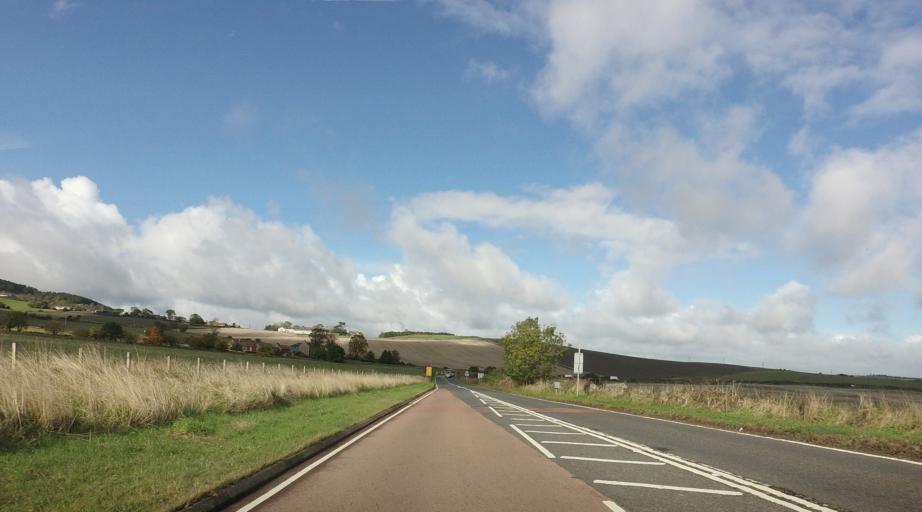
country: GB
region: Scotland
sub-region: Fife
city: Balmullo
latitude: 56.3815
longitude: -2.9228
